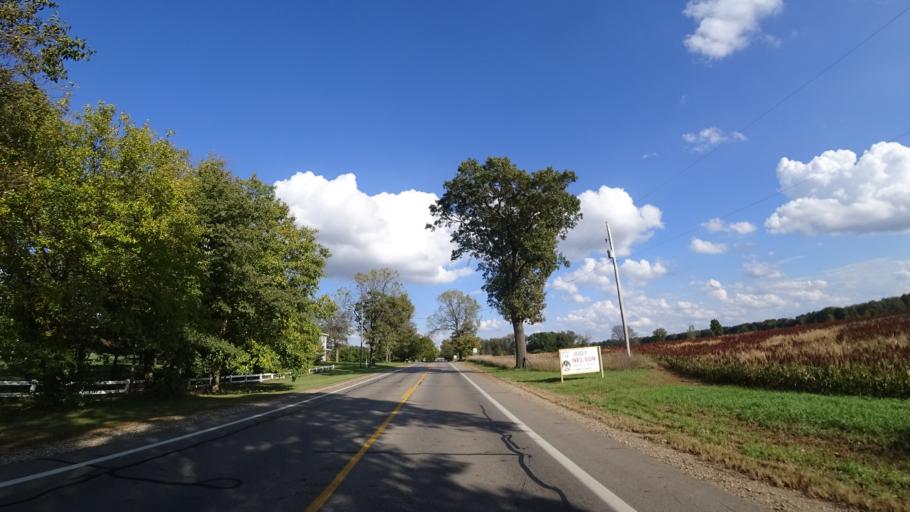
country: US
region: Michigan
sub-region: Saint Joseph County
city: Three Rivers
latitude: 41.9256
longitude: -85.6105
